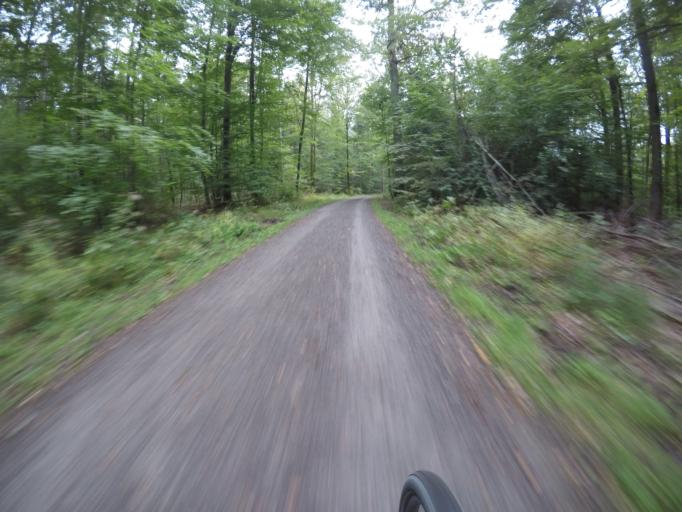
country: DE
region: Baden-Wuerttemberg
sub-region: Regierungsbezirk Stuttgart
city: Gerlingen
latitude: 48.7499
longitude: 9.0580
